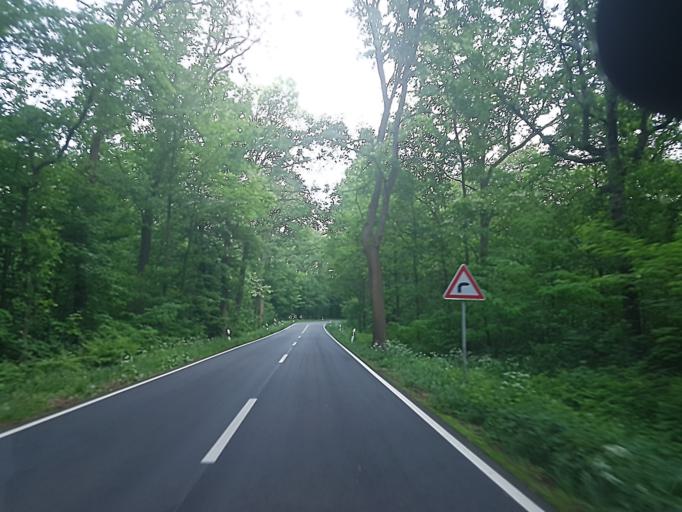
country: DE
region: Saxony-Anhalt
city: Klieken
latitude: 51.9341
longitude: 12.3775
